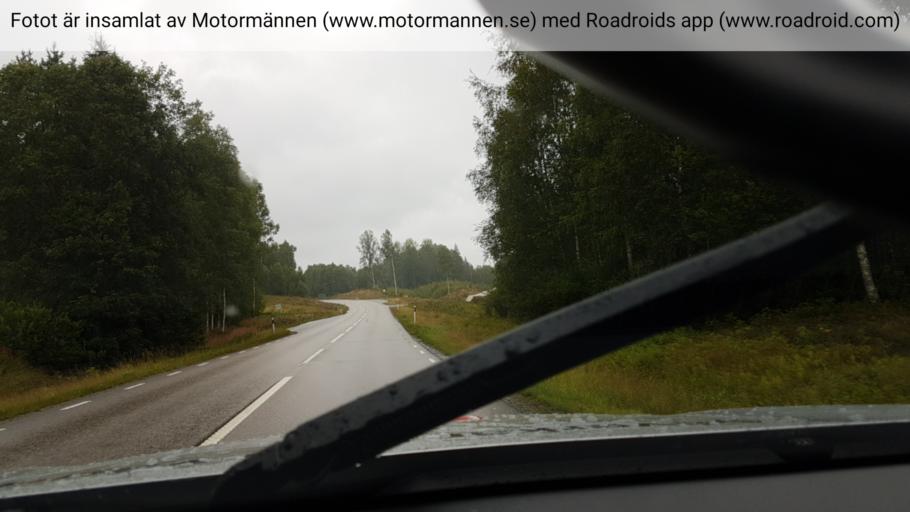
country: SE
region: Vaestra Goetaland
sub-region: Bengtsfors Kommun
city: Dals Langed
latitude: 58.8842
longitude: 12.2119
